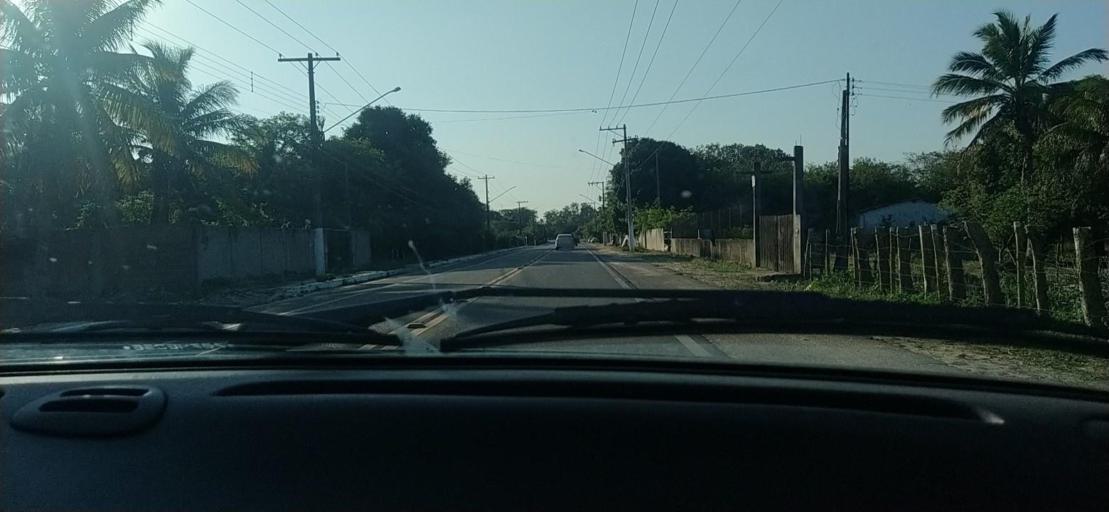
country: BR
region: Espirito Santo
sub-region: Conceicao Da Barra
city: Conceicao da Barra
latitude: -18.5692
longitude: -39.7413
